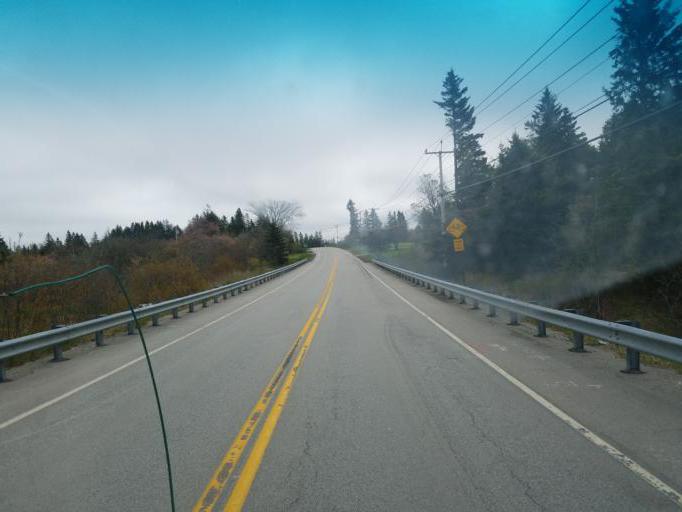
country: US
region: Maine
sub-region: Washington County
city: Eastport
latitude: 44.8139
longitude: -67.0743
